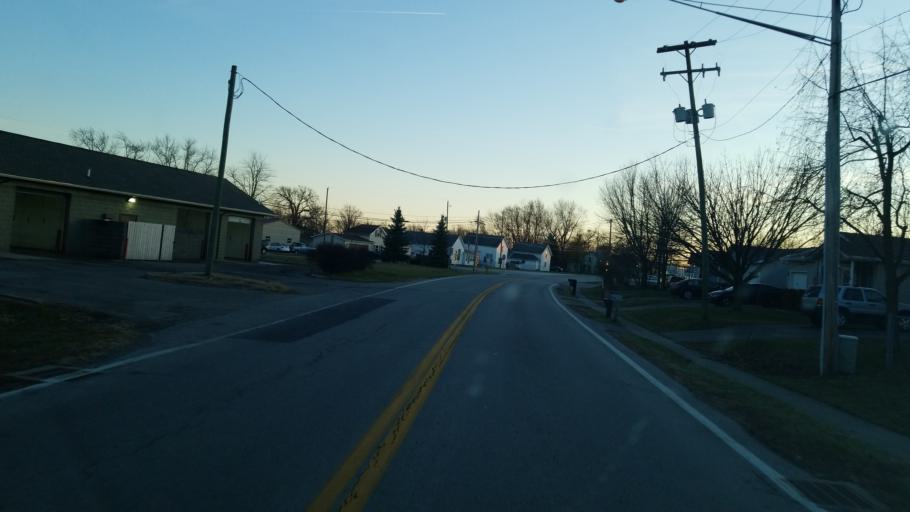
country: US
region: Ohio
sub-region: Madison County
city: Mount Sterling
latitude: 39.7134
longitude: -83.2718
